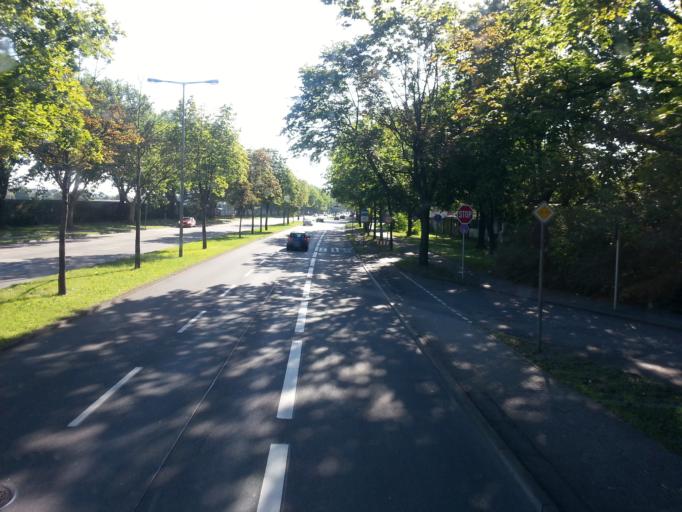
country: DE
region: Berlin
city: Reinickendorf
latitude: 52.5594
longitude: 13.3154
